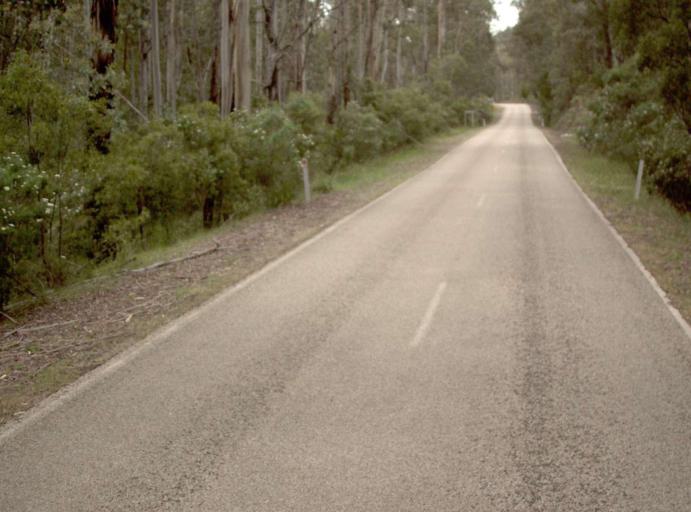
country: AU
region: Victoria
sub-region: East Gippsland
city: Bairnsdale
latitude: -37.6309
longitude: 147.2199
